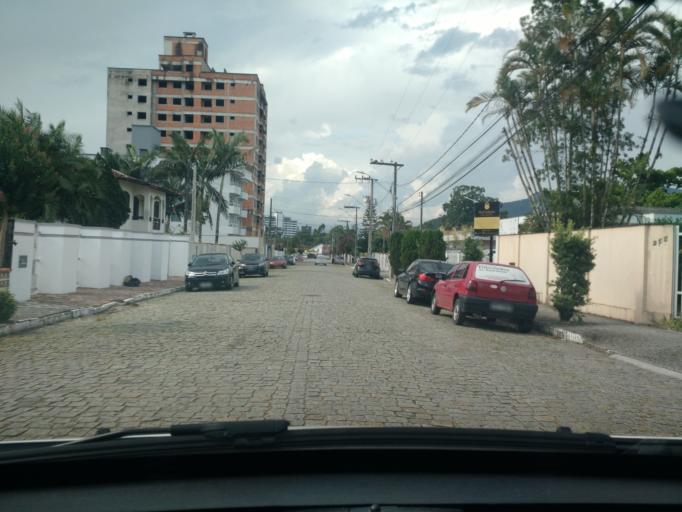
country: BR
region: Santa Catarina
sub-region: Jaragua Do Sul
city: Jaragua do Sul
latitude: -26.5032
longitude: -49.0875
